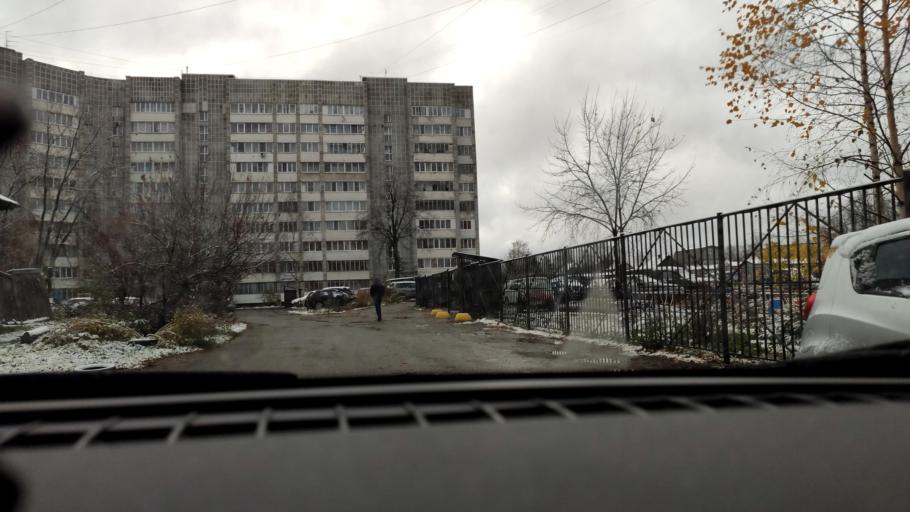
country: RU
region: Perm
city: Perm
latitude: 58.0290
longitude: 56.3265
